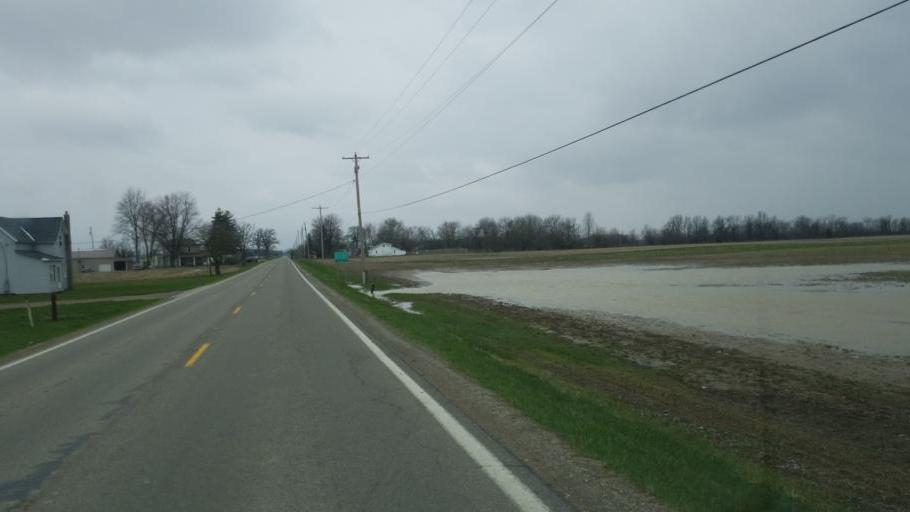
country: US
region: Ohio
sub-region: Union County
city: Richwood
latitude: 40.4253
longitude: -83.3085
